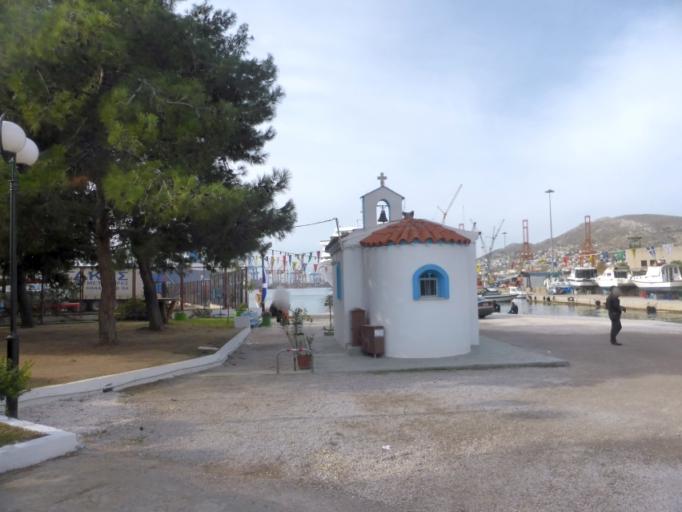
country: GR
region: Attica
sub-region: Nomos Piraios
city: Drapetsona
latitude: 37.9525
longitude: 23.6095
